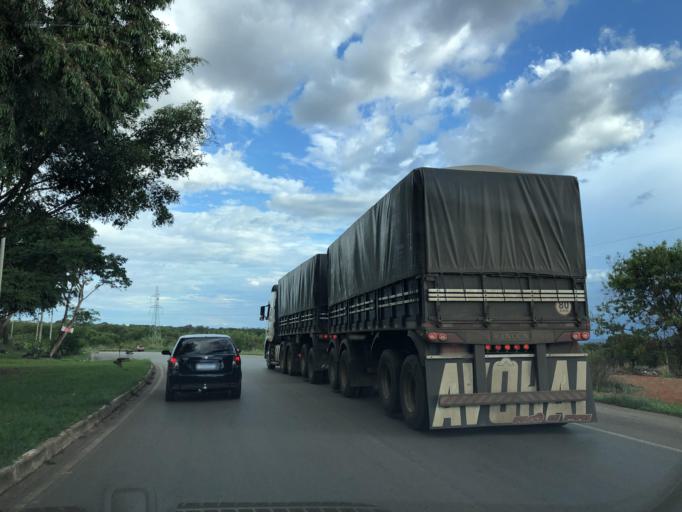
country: BR
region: Goias
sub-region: Luziania
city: Luziania
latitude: -16.0413
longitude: -48.0619
